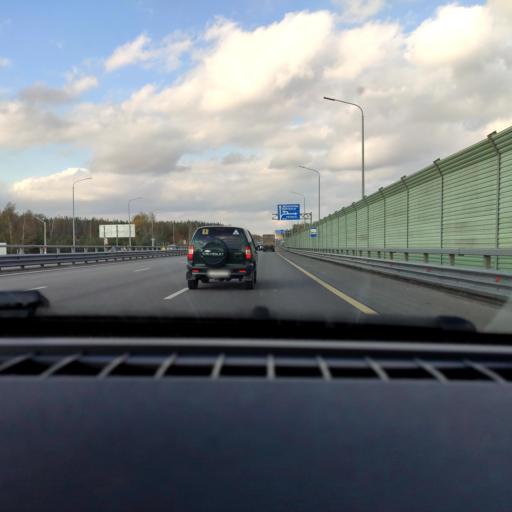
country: RU
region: Voronezj
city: Somovo
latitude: 51.6835
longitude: 39.3021
